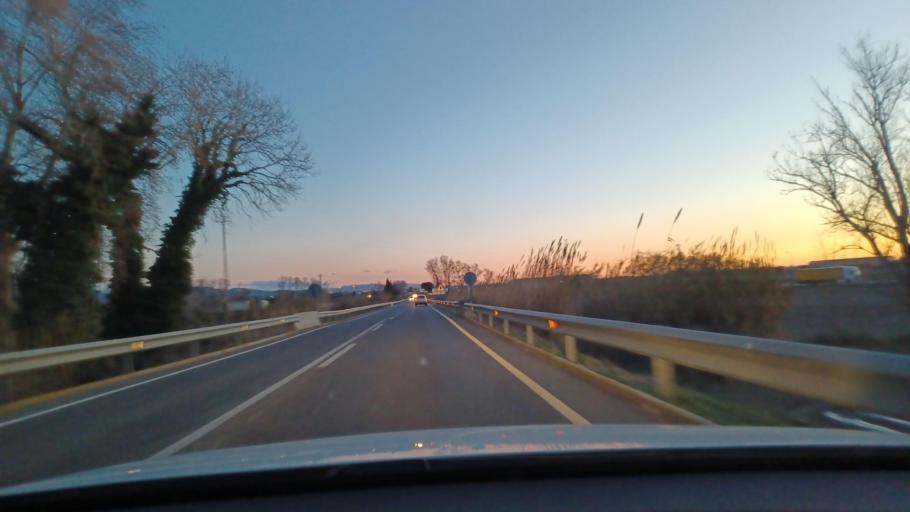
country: ES
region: Catalonia
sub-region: Provincia de Tarragona
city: Amposta
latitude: 40.7169
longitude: 0.5839
